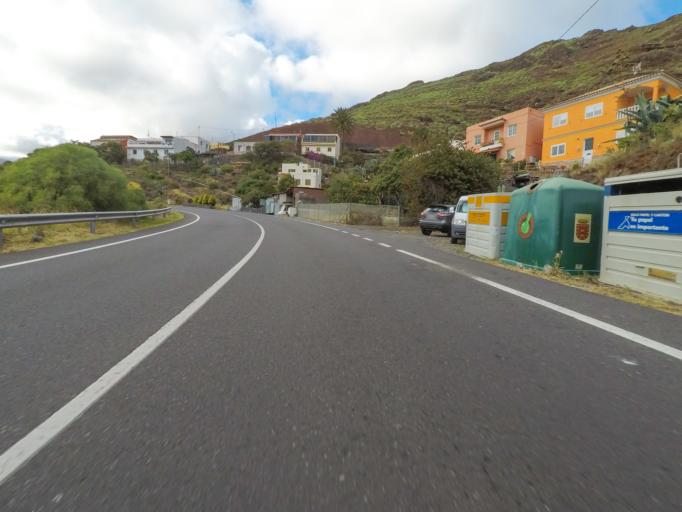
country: ES
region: Canary Islands
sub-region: Provincia de Santa Cruz de Tenerife
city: San Sebastian de la Gomera
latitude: 28.1105
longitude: -17.1271
